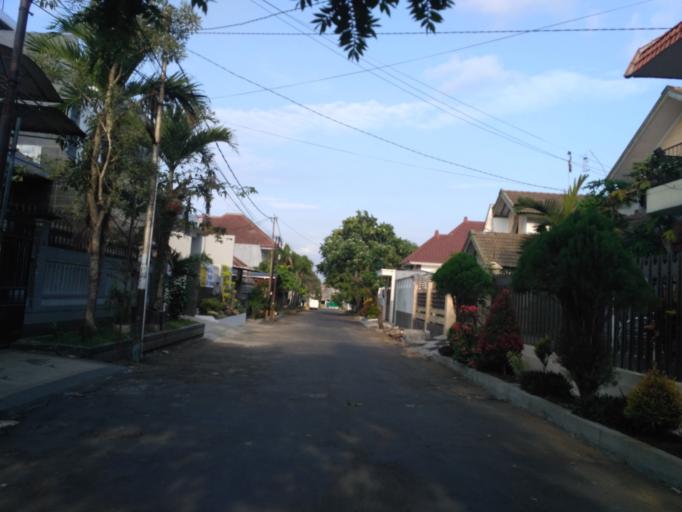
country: ID
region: East Java
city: Malang
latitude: -7.9363
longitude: 112.6345
